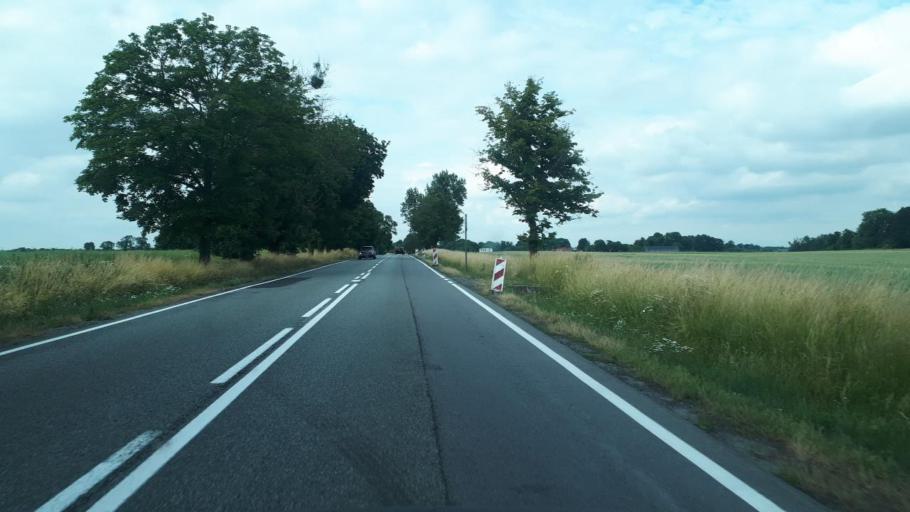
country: PL
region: Opole Voivodeship
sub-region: Powiat kluczborski
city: Byczyna
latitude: 51.0543
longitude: 18.1975
